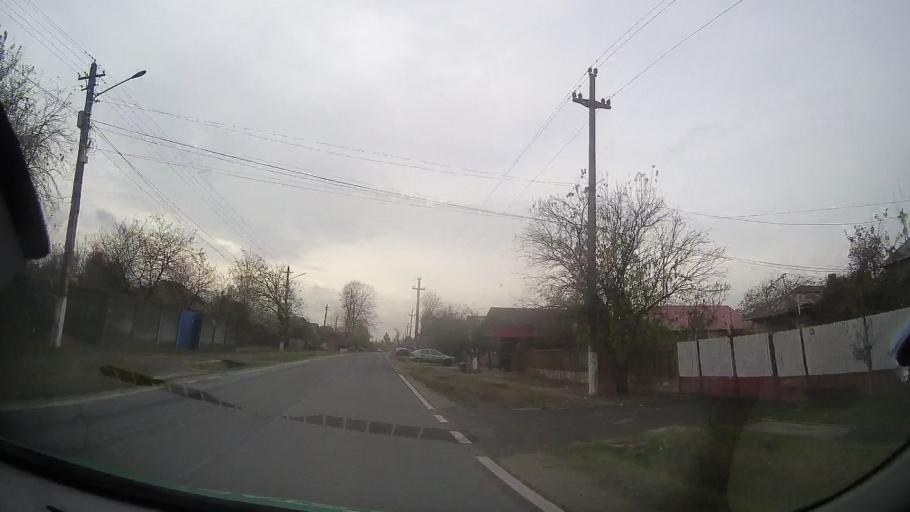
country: RO
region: Ilfov
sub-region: Comuna Gruiu
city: Silistea Snagovului
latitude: 44.7471
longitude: 26.1850
